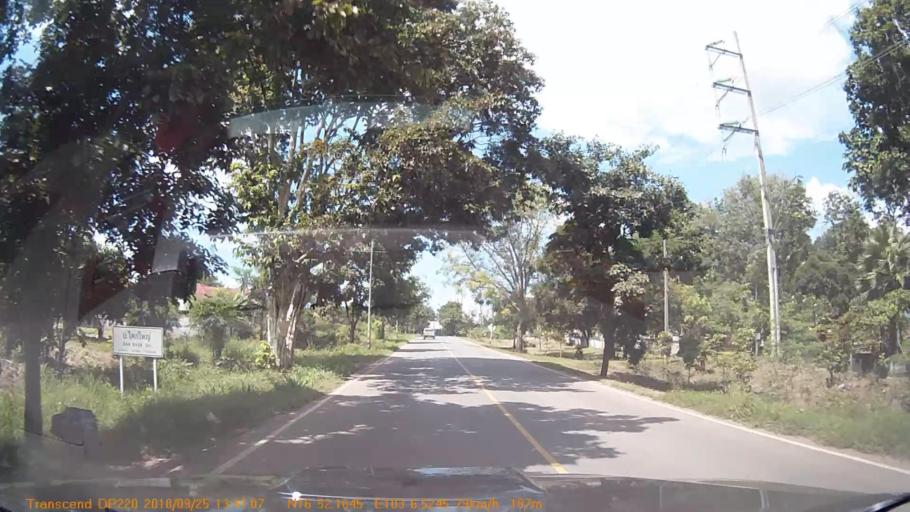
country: TH
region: Changwat Udon Thani
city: Si That
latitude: 16.8696
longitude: 103.1088
